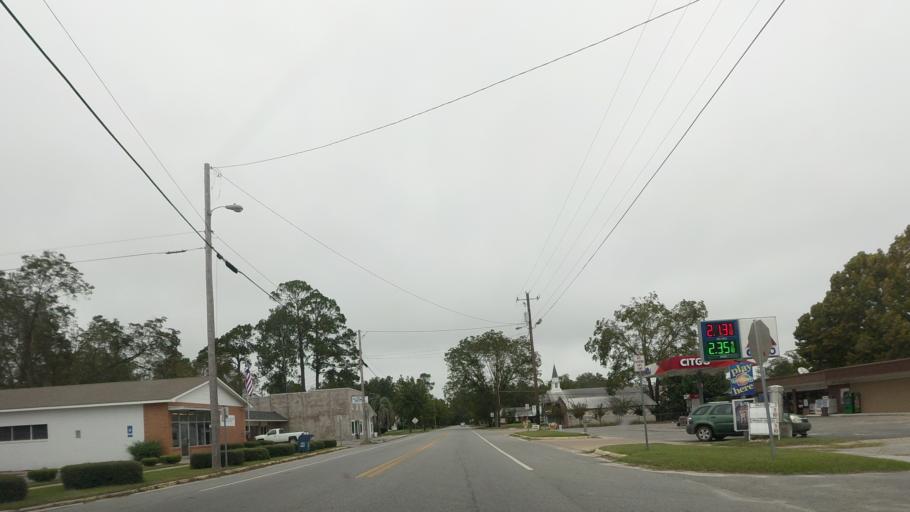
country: US
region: Georgia
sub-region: Berrien County
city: Enigma
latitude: 31.3817
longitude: -83.2240
